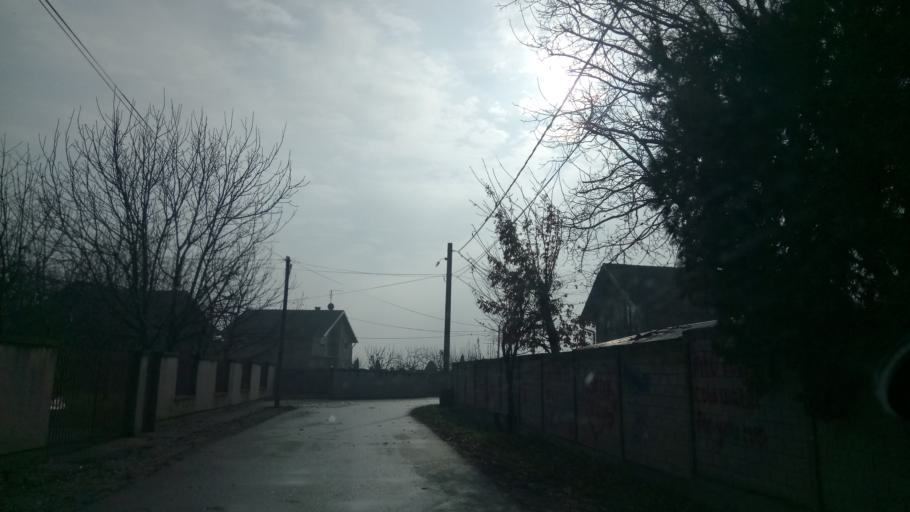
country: RS
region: Autonomna Pokrajina Vojvodina
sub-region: Sremski Okrug
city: Stara Pazova
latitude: 44.9840
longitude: 20.1830
